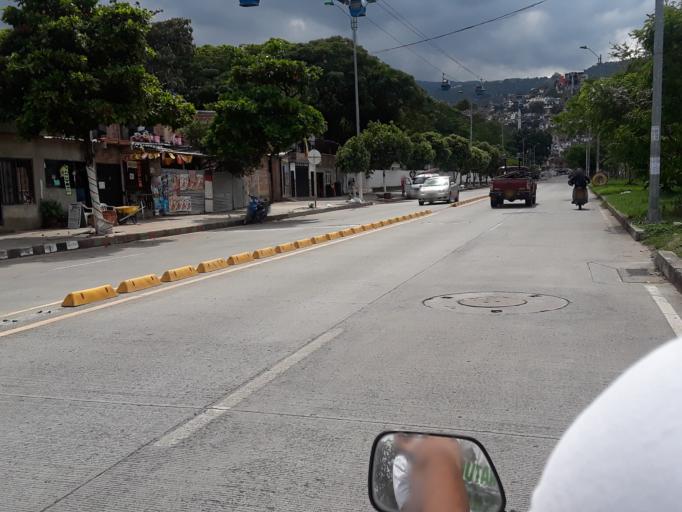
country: CO
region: Valle del Cauca
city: Cali
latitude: 3.4162
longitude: -76.5504
